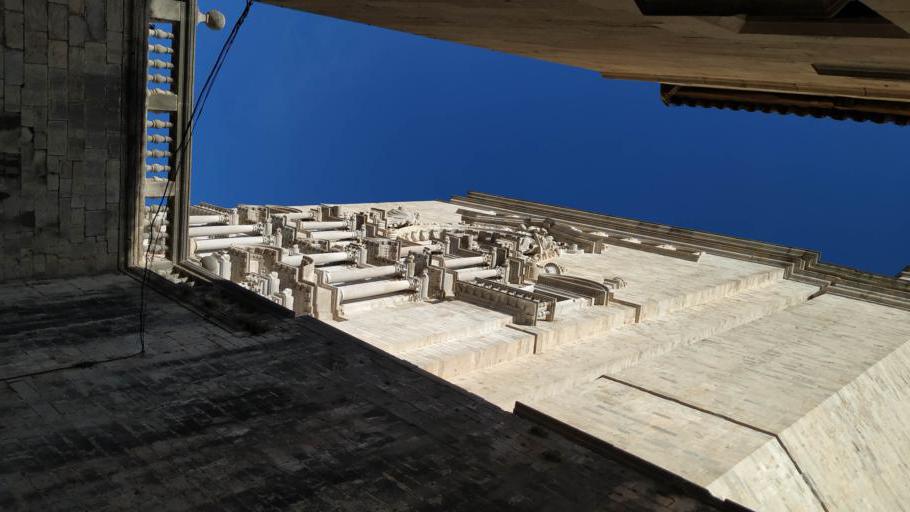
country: ES
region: Catalonia
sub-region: Provincia de Girona
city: Girona
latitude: 41.9871
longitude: 2.8258
